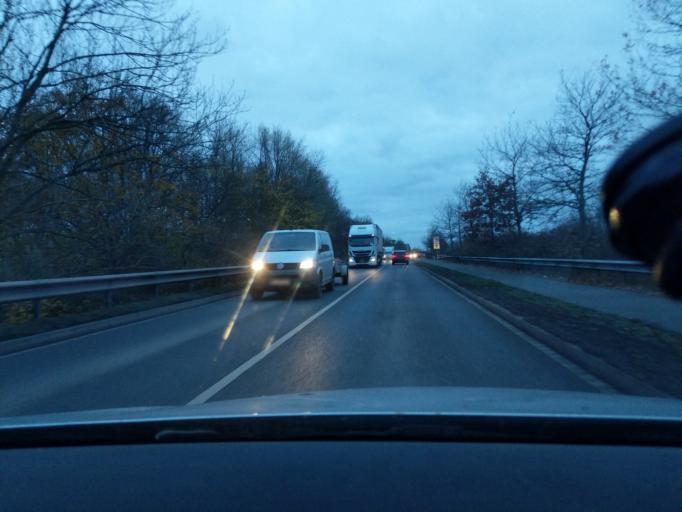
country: DE
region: North Rhine-Westphalia
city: Lunen
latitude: 51.6076
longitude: 7.4806
